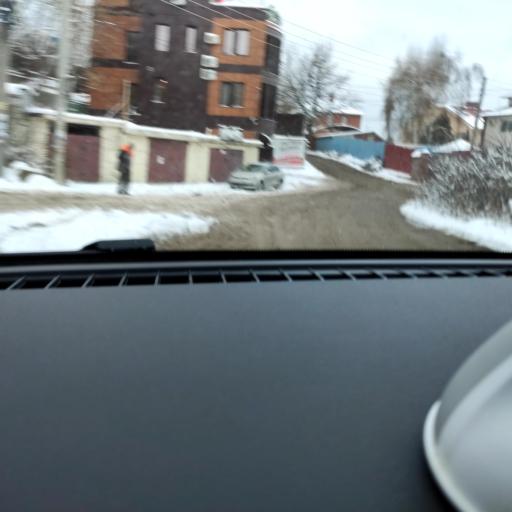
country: RU
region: Samara
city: Samara
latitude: 53.2428
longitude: 50.1711
